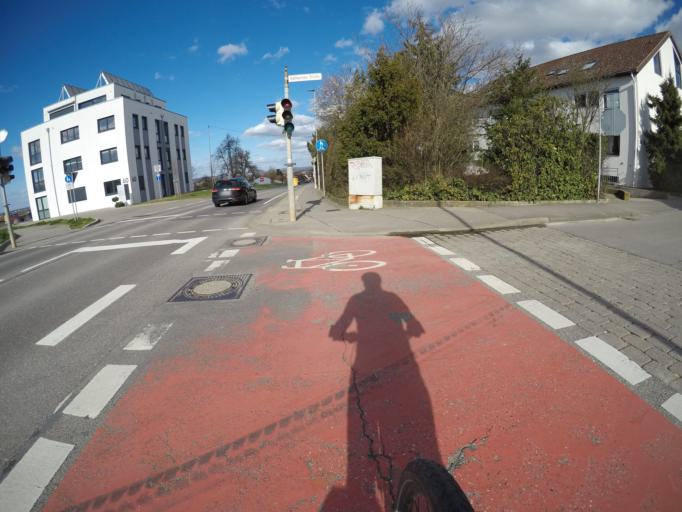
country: DE
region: Baden-Wuerttemberg
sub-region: Regierungsbezirk Stuttgart
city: Filderstadt
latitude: 48.6710
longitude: 9.2325
